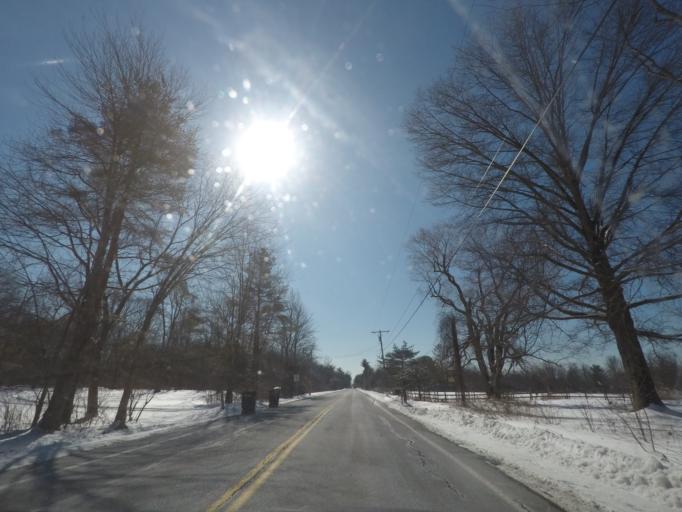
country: US
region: New York
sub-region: Saratoga County
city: Ballston Spa
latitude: 42.9831
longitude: -73.8327
